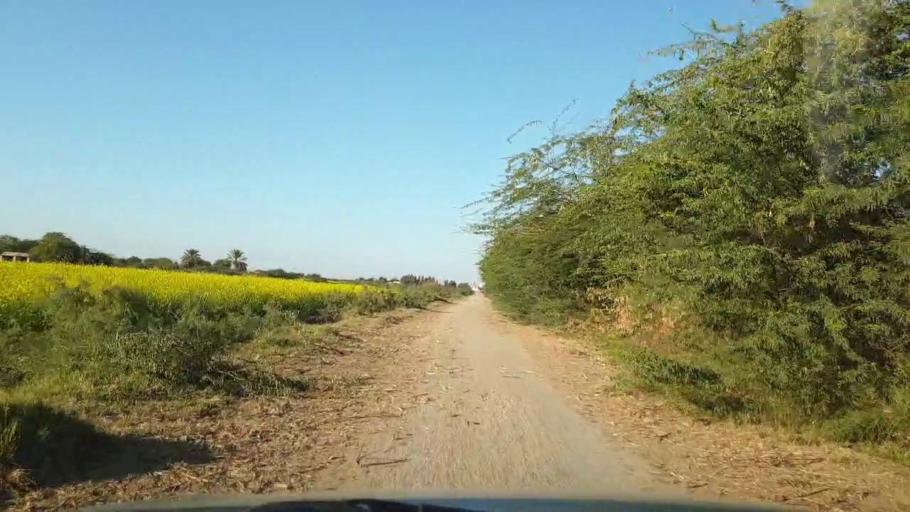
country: PK
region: Sindh
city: Jhol
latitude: 25.9029
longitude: 68.9250
